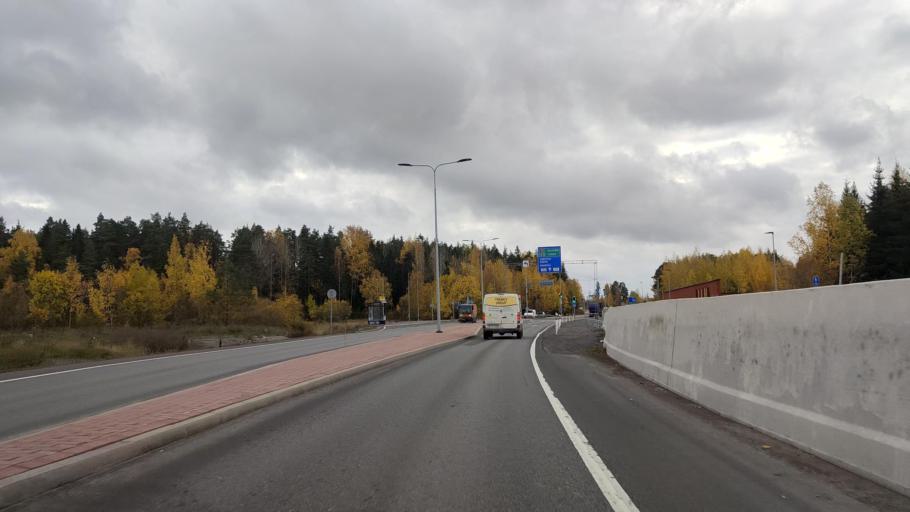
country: FI
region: Varsinais-Suomi
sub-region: Turku
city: Kaarina
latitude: 60.4295
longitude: 22.3842
